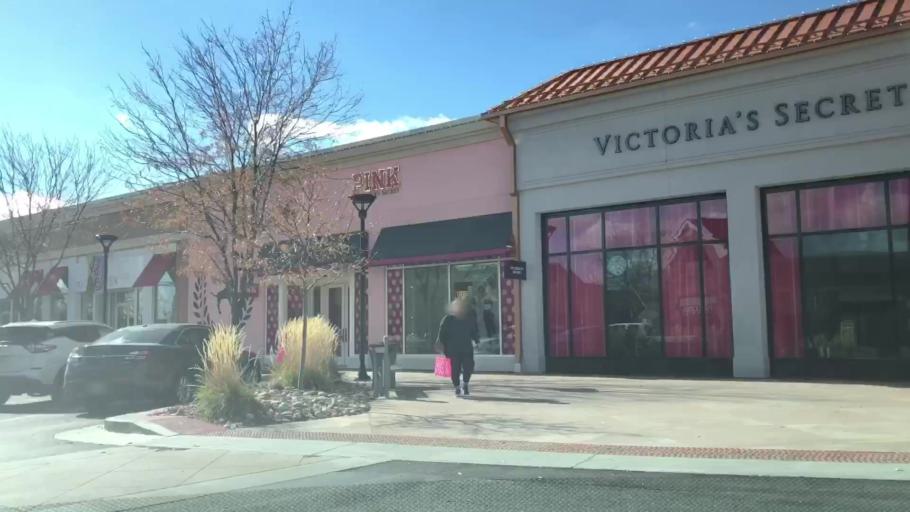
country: US
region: Colorado
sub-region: Larimer County
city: Loveland
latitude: 40.4167
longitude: -104.9896
